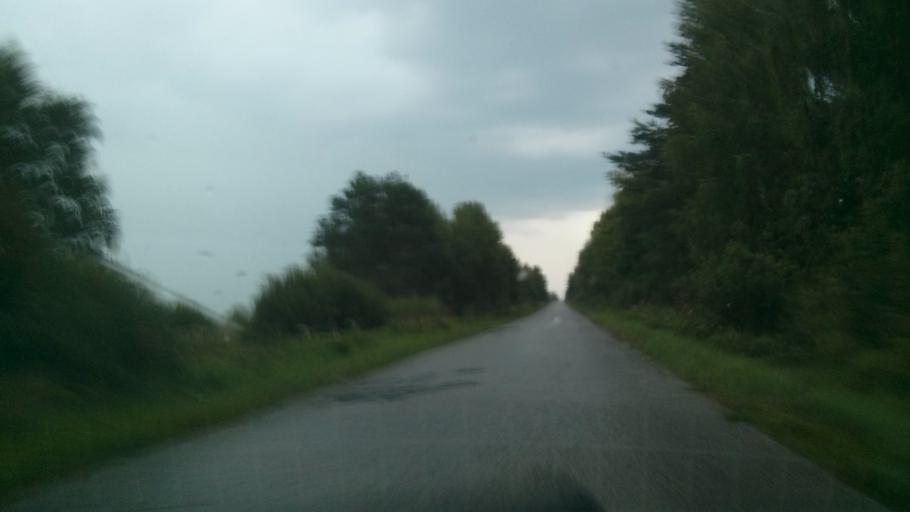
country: RU
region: Nizjnij Novgorod
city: Shimorskoye
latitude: 55.3390
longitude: 41.8797
